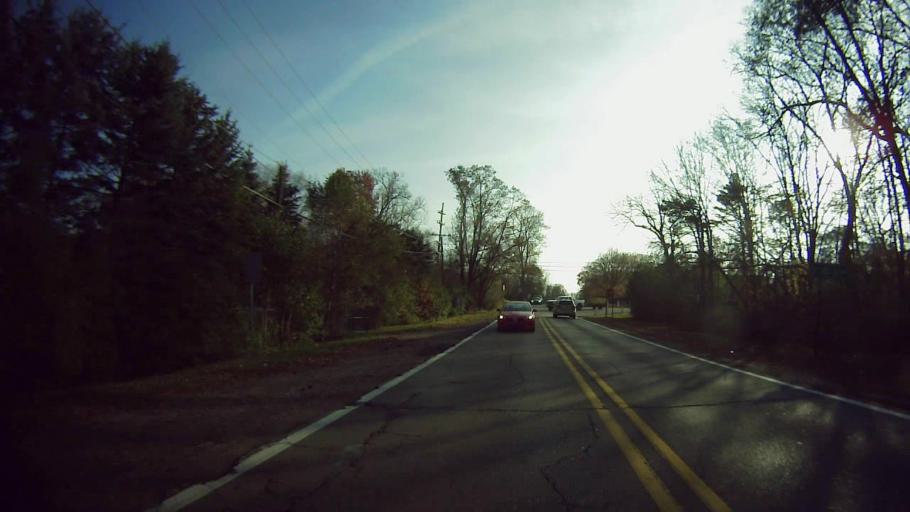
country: US
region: Michigan
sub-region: Oakland County
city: Beverly Hills
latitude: 42.5309
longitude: -83.2448
